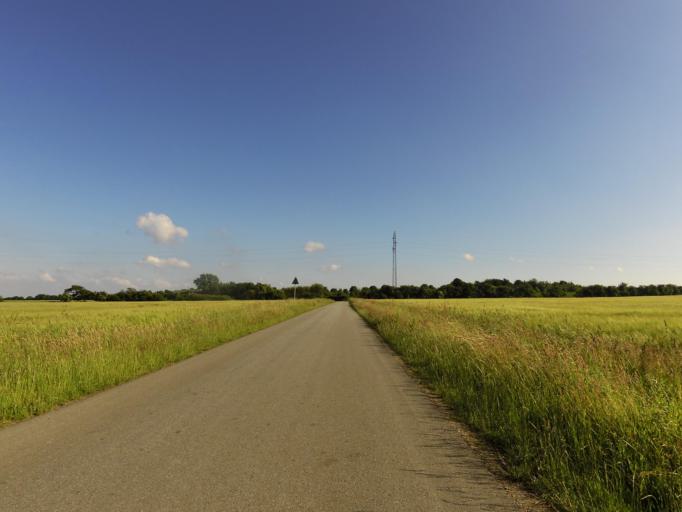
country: DK
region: South Denmark
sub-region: Vejen Kommune
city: Rodding
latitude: 55.3503
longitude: 9.1034
